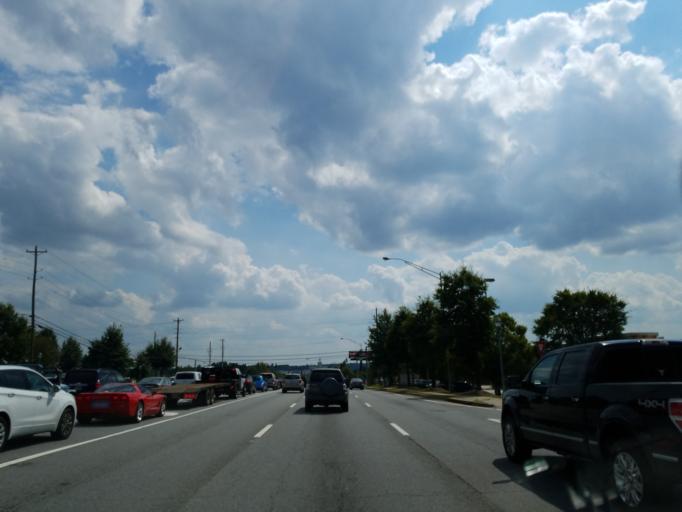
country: US
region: Georgia
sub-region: Gwinnett County
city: Buford
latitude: 34.0766
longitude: -83.9837
